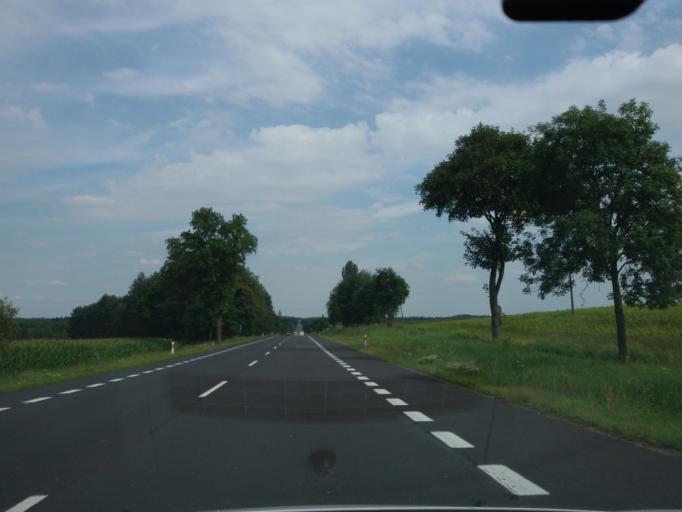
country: PL
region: Lower Silesian Voivodeship
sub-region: Powiat polkowicki
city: Gaworzyce
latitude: 51.6582
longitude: 15.8314
